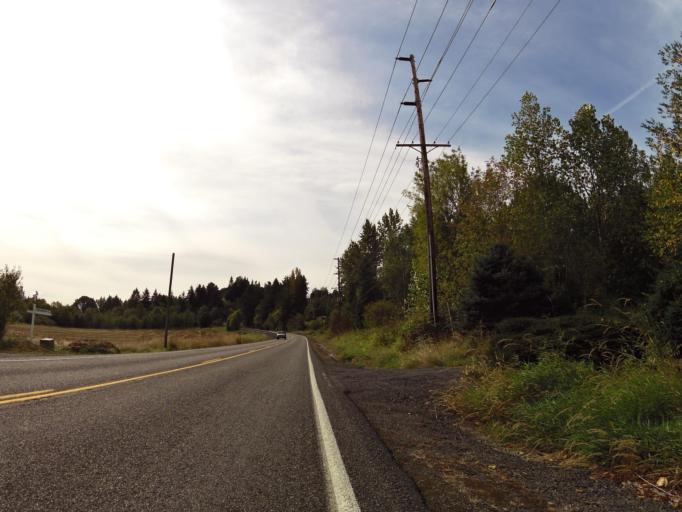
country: US
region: Washington
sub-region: Lewis County
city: Chehalis
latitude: 46.6375
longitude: -122.9714
